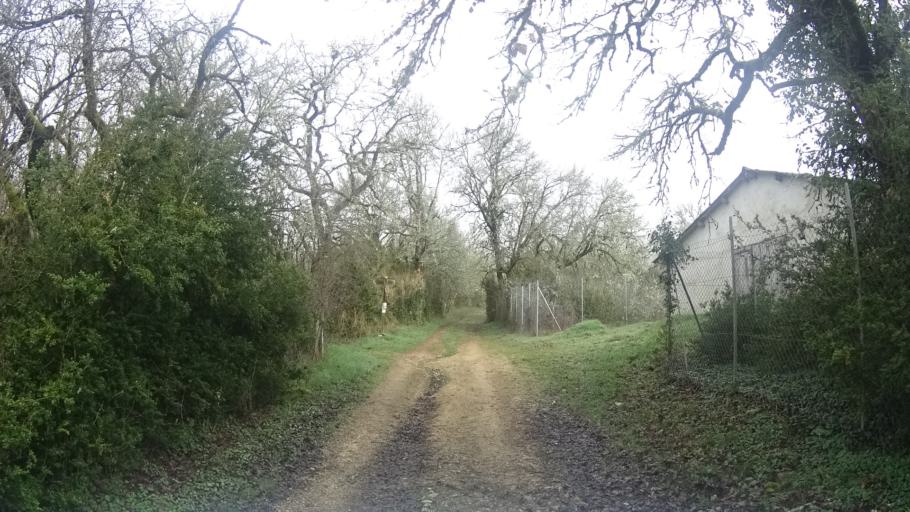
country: FR
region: Aquitaine
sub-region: Departement de la Dordogne
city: Terrasson-Lavilledieu
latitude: 45.1045
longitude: 1.2656
